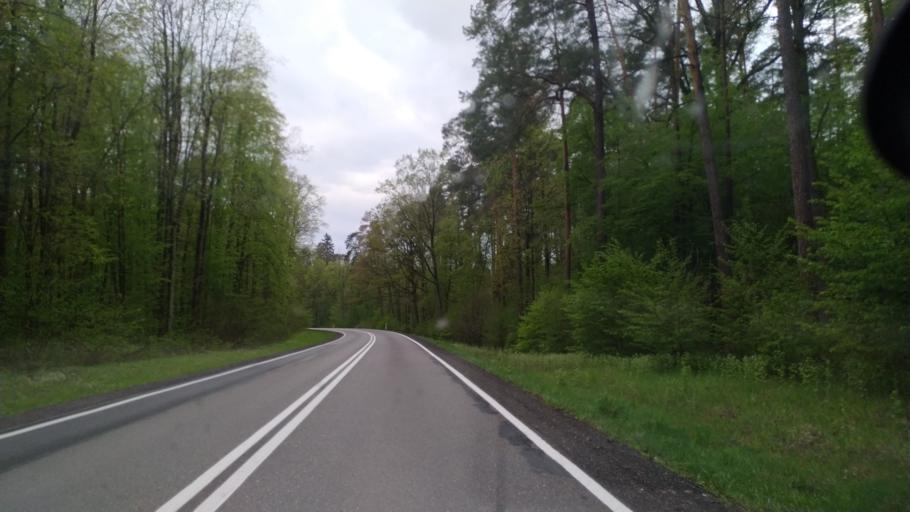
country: PL
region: Pomeranian Voivodeship
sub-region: Powiat kwidzynski
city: Ryjewo
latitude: 53.8123
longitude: 18.9731
